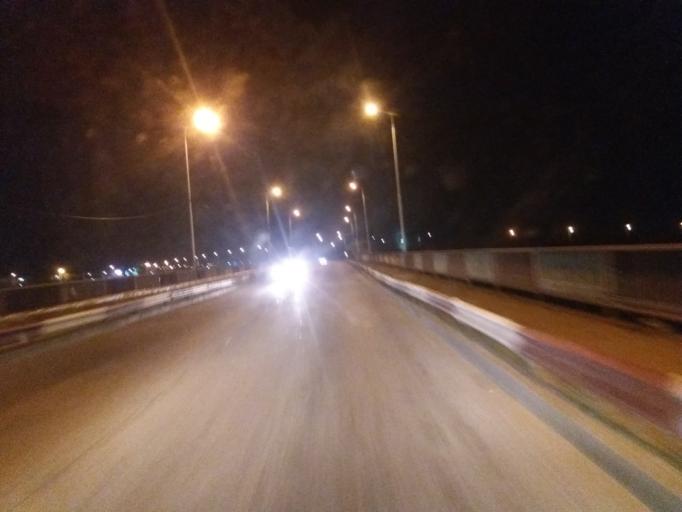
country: RO
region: Constanta
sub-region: Comuna Navodari
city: Navodari
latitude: 44.3212
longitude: 28.6245
